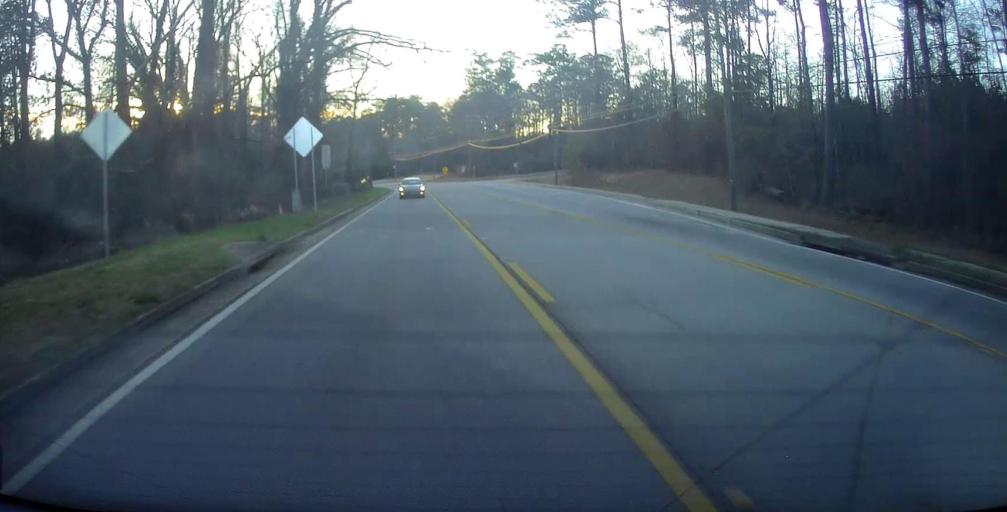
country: US
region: Georgia
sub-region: Troup County
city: La Grange
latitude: 33.0571
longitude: -84.9884
